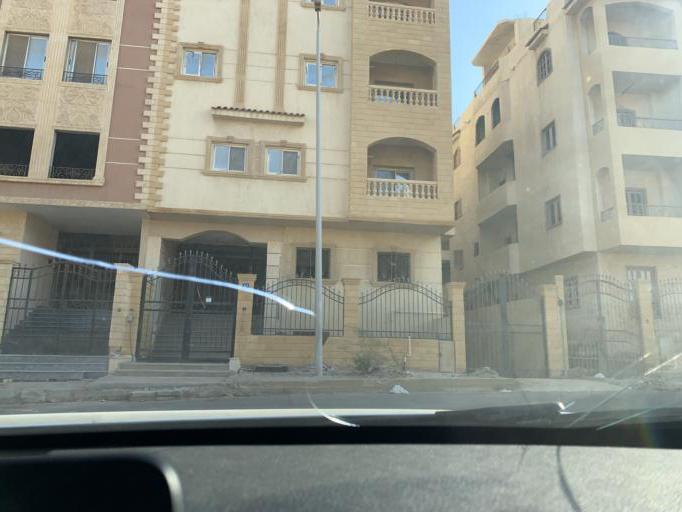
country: EG
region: Muhafazat al Qalyubiyah
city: Al Khankah
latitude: 30.0018
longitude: 31.4867
